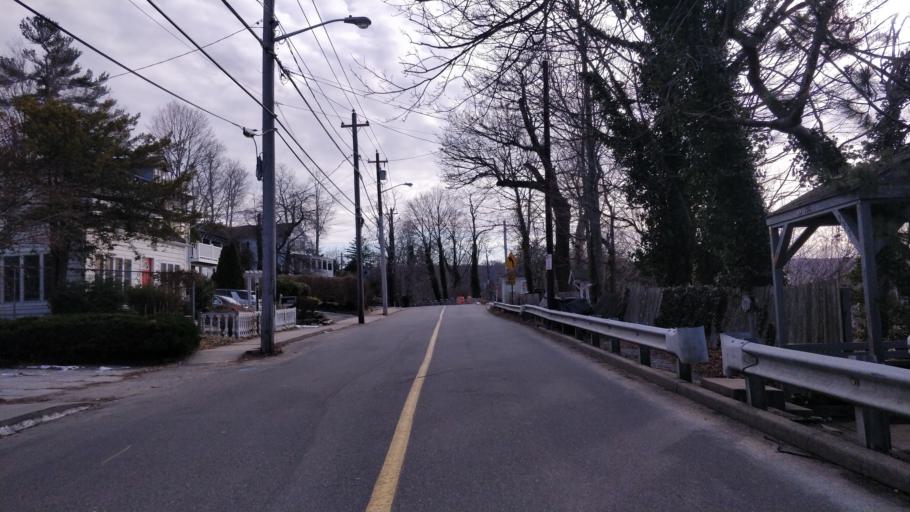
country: US
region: New York
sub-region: Suffolk County
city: Northport
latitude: 40.8959
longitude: -73.3529
